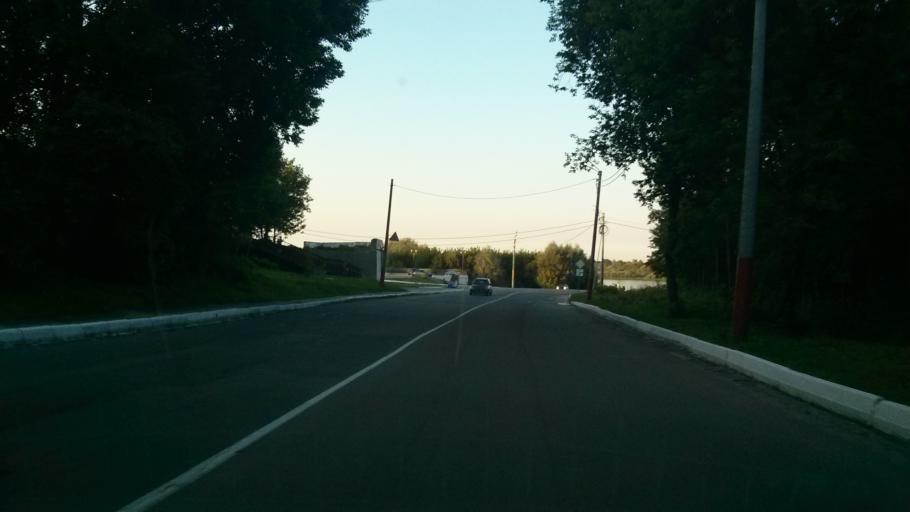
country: RU
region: Vladimir
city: Murom
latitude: 55.5793
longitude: 42.0612
